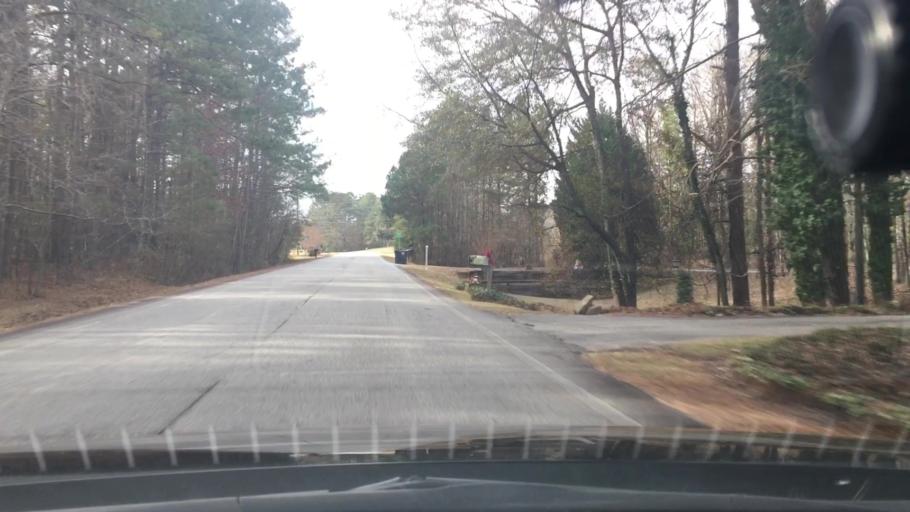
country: US
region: Georgia
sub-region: Coweta County
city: Senoia
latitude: 33.2874
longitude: -84.4432
